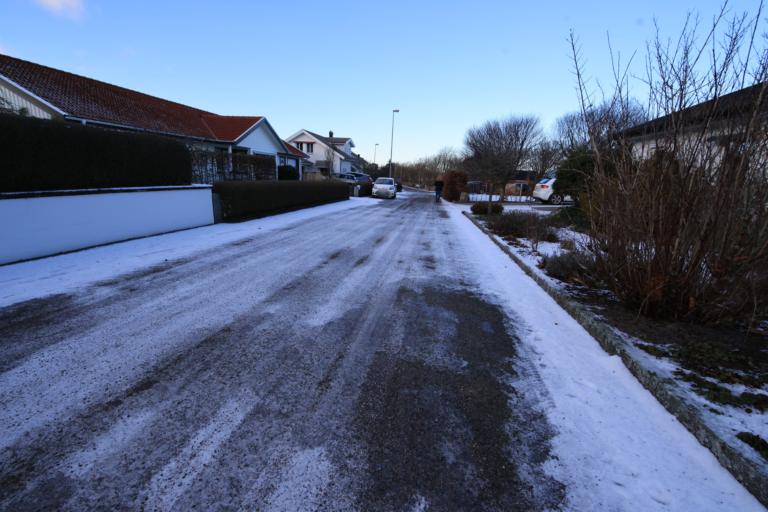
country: SE
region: Halland
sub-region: Varbergs Kommun
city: Traslovslage
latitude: 57.0610
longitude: 12.2858
